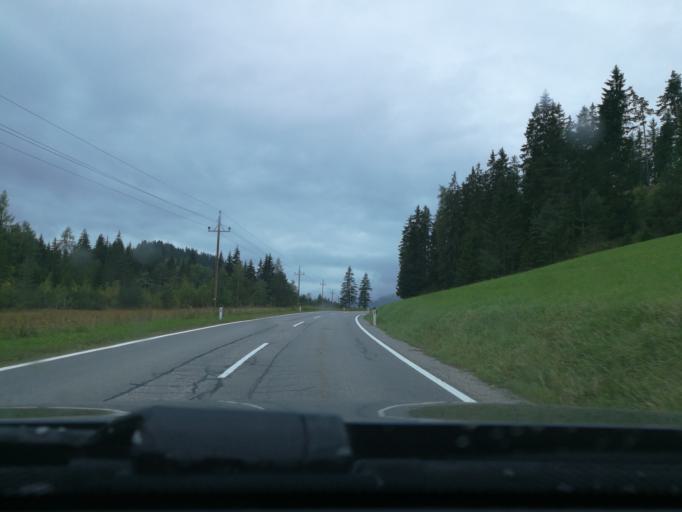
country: AT
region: Salzburg
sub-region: Politischer Bezirk Sankt Johann im Pongau
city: Forstau
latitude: 47.3779
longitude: 13.5171
